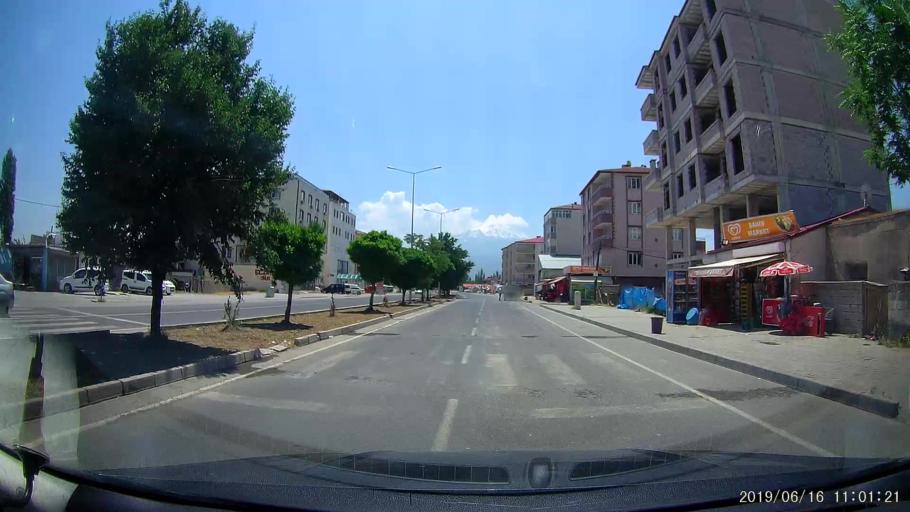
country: TR
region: Igdir
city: Igdir
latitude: 39.9155
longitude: 44.0491
